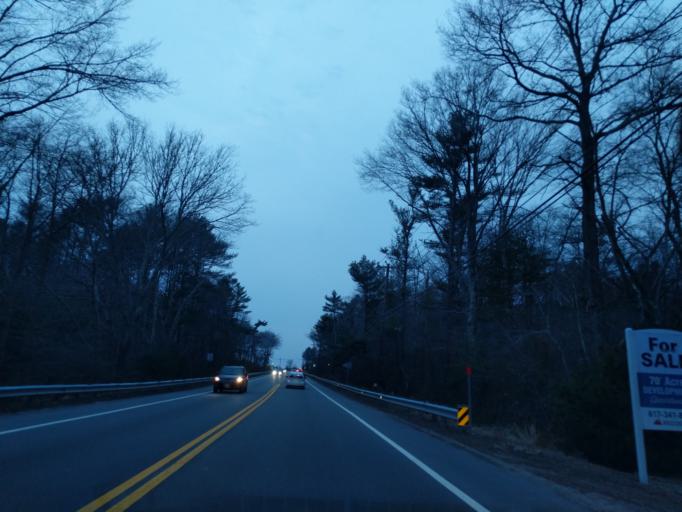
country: US
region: Massachusetts
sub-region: Bristol County
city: Raynham Center
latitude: 41.9036
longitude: -70.9992
